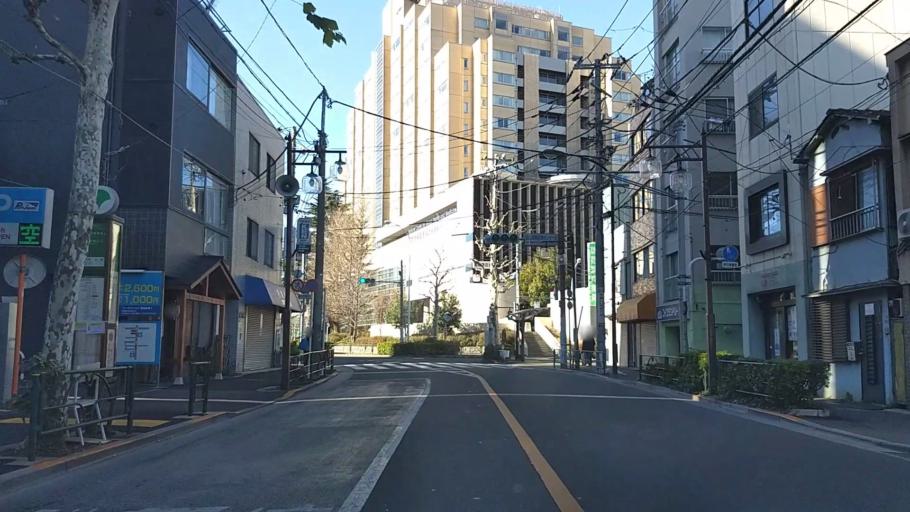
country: JP
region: Tokyo
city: Tokyo
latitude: 35.7012
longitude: 139.7180
